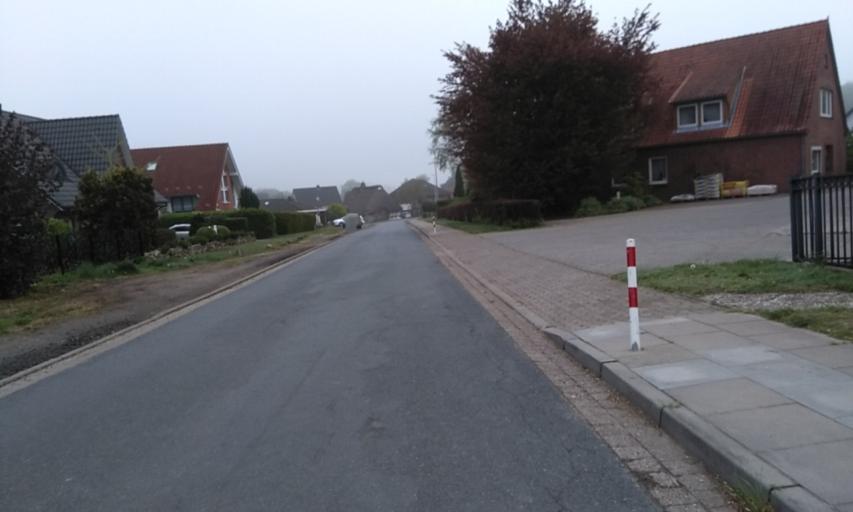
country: DE
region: Lower Saxony
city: Nottensdorf
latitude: 53.4769
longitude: 9.6168
